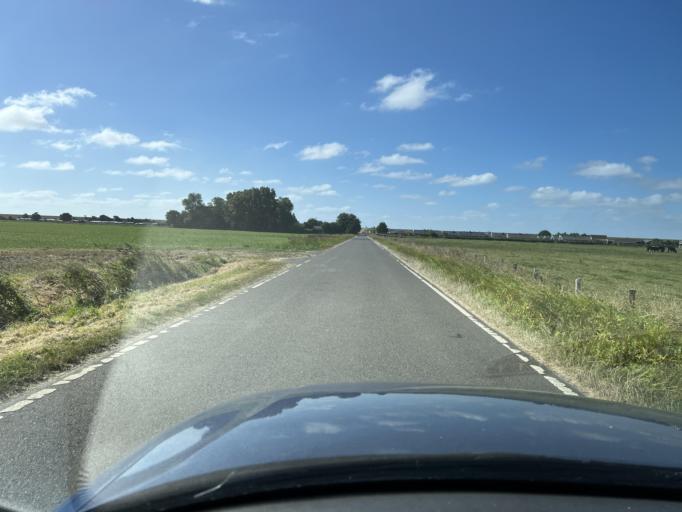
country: DE
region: Schleswig-Holstein
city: Wesselburenerkoog
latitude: 54.2467
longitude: 8.8482
